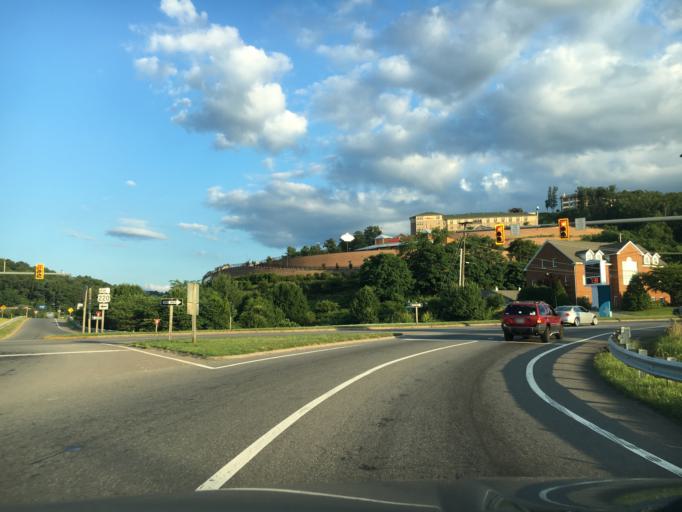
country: US
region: Virginia
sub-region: Roanoke County
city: Narrows
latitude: 37.2318
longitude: -79.9741
